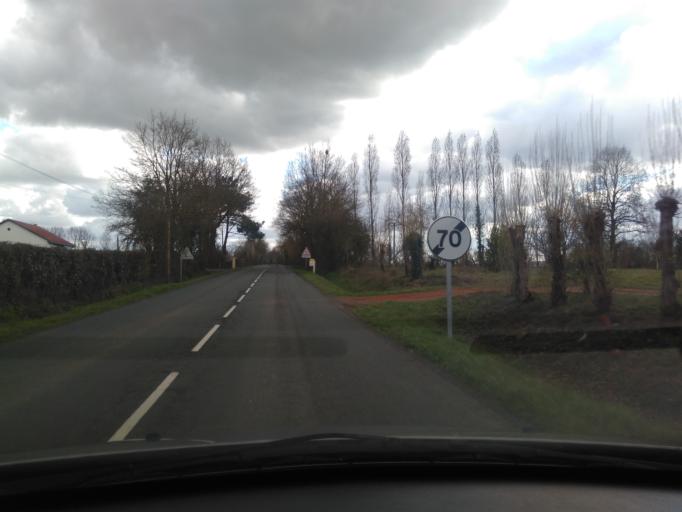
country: FR
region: Pays de la Loire
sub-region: Departement de la Vendee
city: Les Essarts
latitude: 46.7580
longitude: -1.2208
